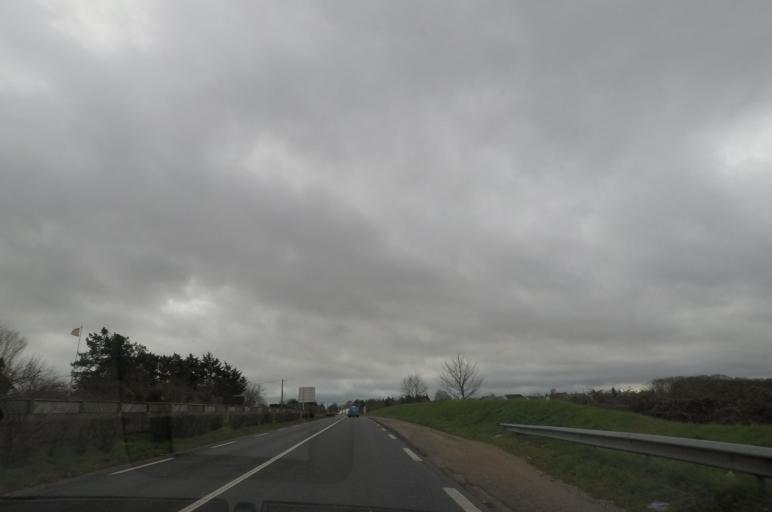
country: FR
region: Centre
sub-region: Departement du Loir-et-Cher
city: Saint-Sulpice-de-Pommeray
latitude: 47.6477
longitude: 1.2750
